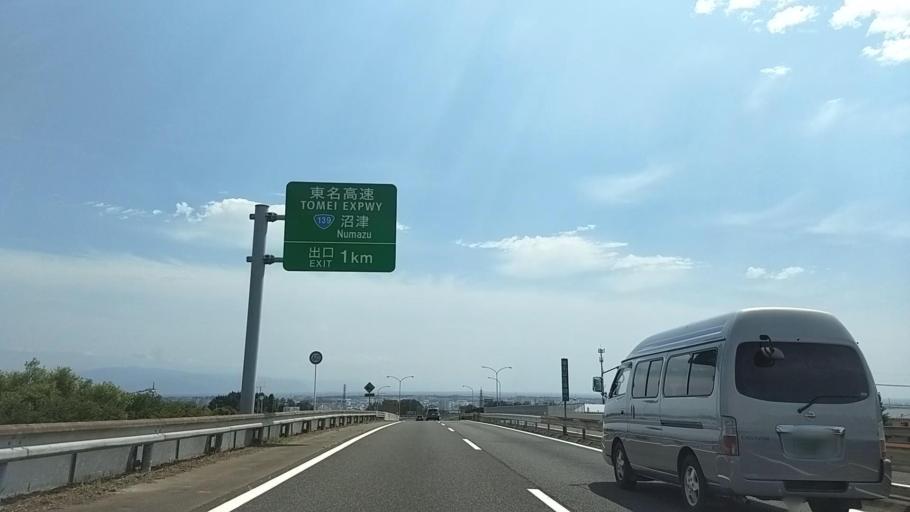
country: JP
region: Shizuoka
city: Fuji
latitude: 35.1854
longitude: 138.6757
